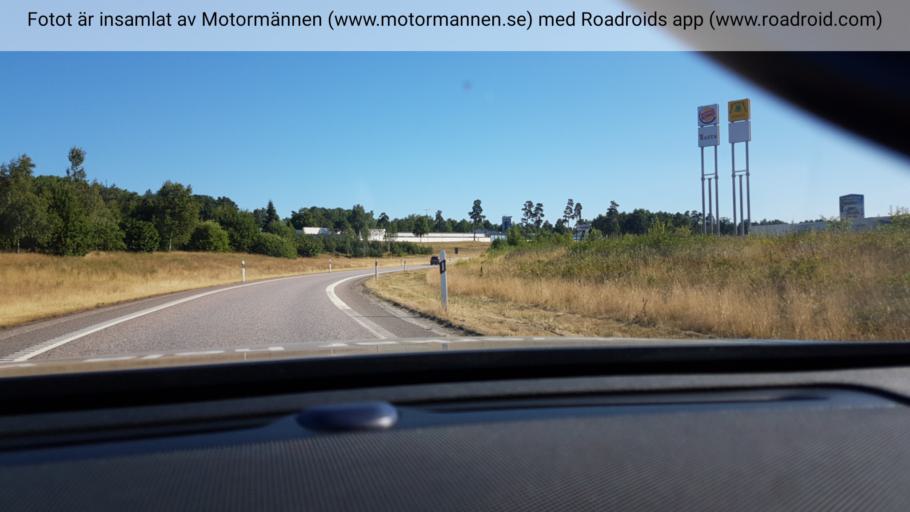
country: SE
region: Kronoberg
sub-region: Markaryds Kommun
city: Markaryd
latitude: 56.4468
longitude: 13.6029
